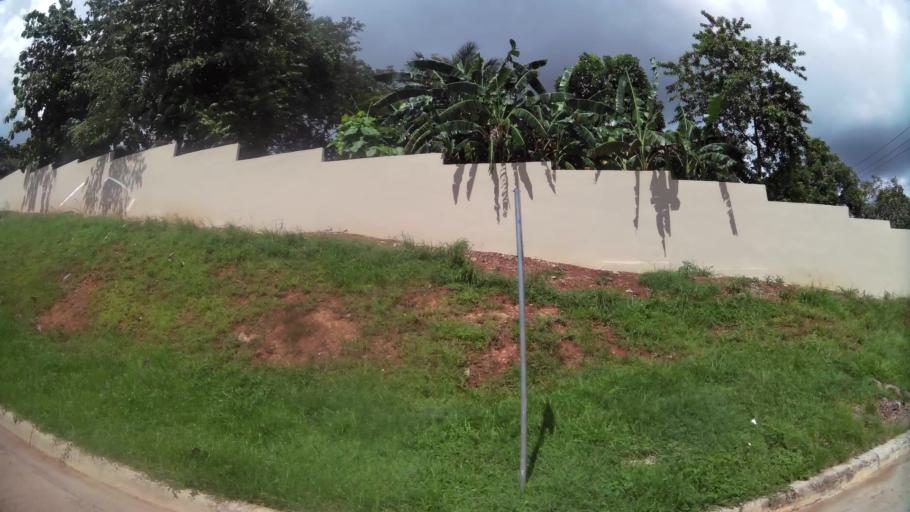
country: PA
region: Panama
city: Vista Alegre
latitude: 8.9243
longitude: -79.7045
